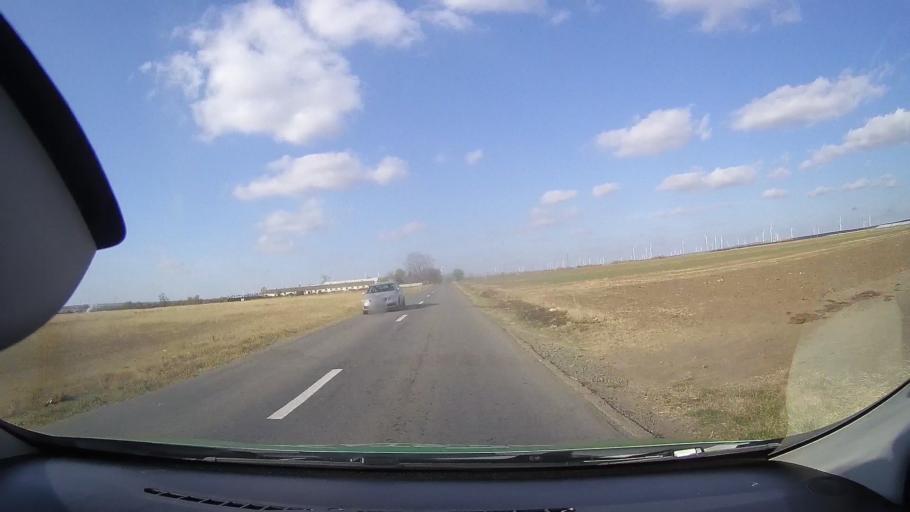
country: RO
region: Constanta
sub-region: Comuna Cogealac
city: Tariverde
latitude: 44.5598
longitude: 28.6101
